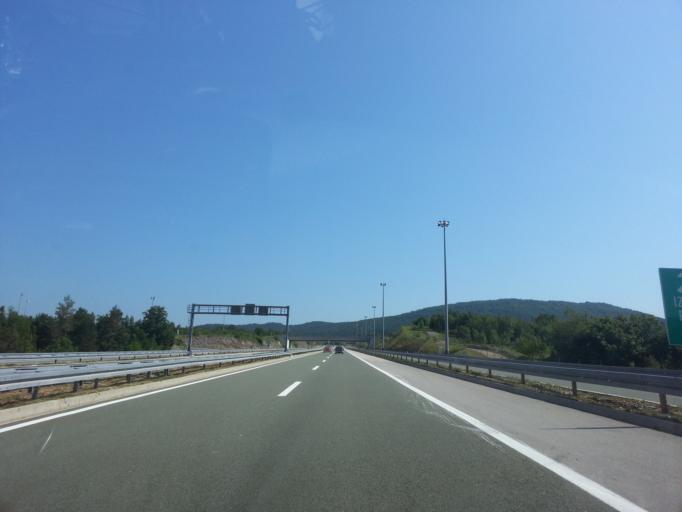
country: HR
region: Primorsko-Goranska
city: Klana
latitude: 45.4705
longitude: 14.2739
